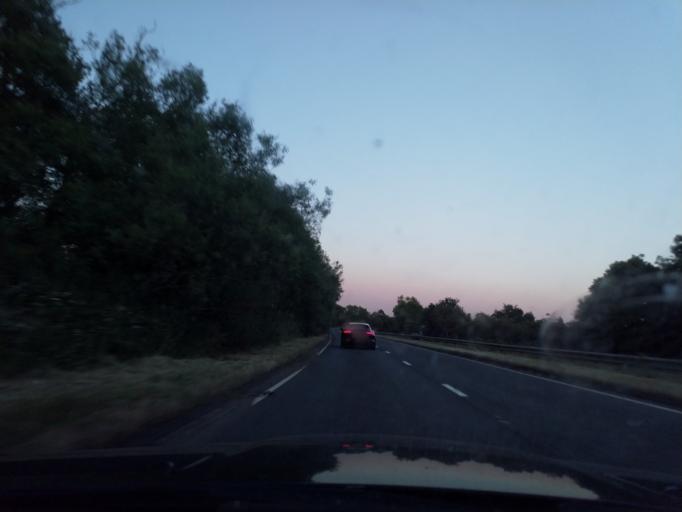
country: GB
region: England
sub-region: Solihull
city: Hampton in Arden
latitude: 52.4383
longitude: -1.6811
